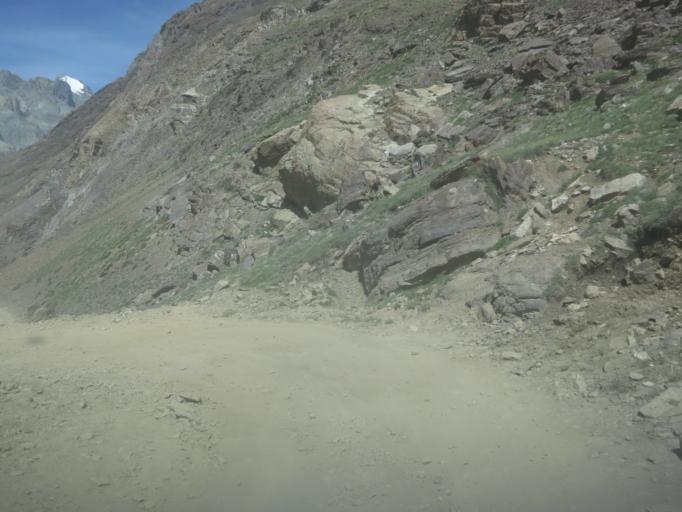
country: IN
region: Himachal Pradesh
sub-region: Kulu
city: Manali
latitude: 32.4368
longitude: 77.6816
